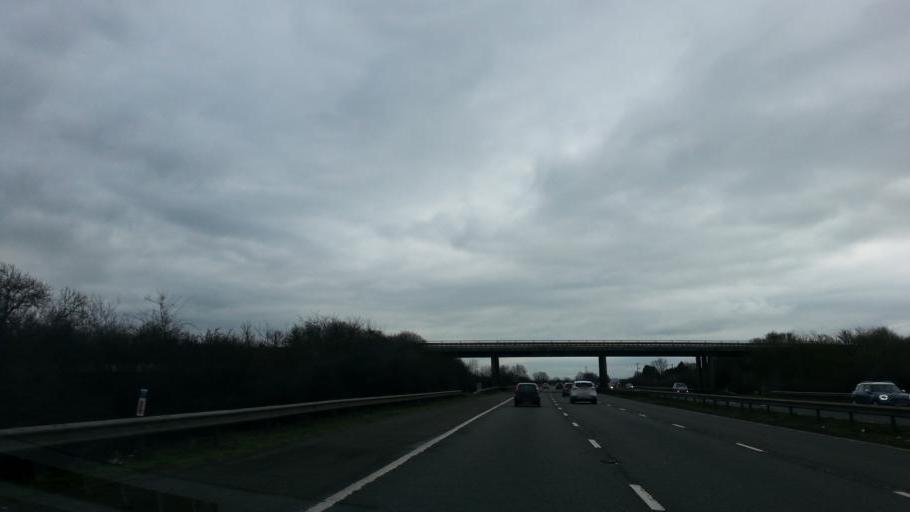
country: GB
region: England
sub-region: Somerset
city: Puriton
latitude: 51.1440
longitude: -2.9739
